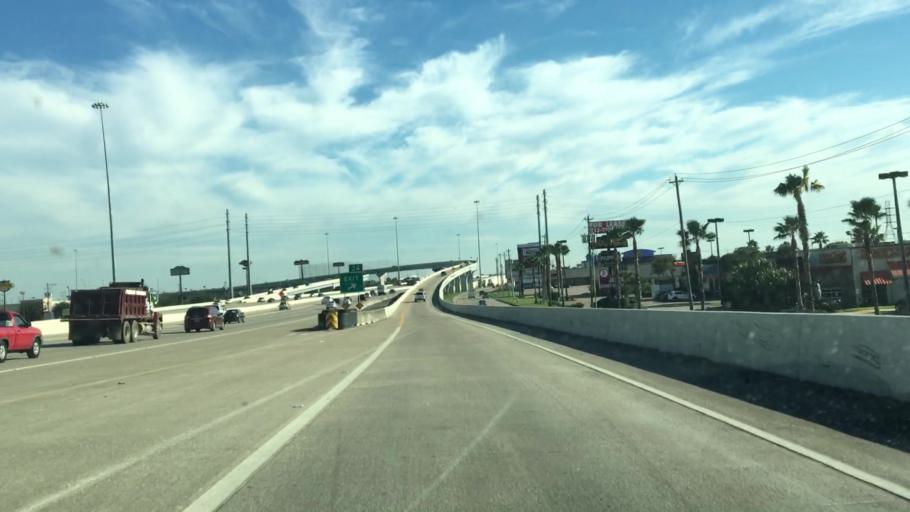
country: US
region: Texas
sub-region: Harris County
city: Webster
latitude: 29.5270
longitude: -95.1275
